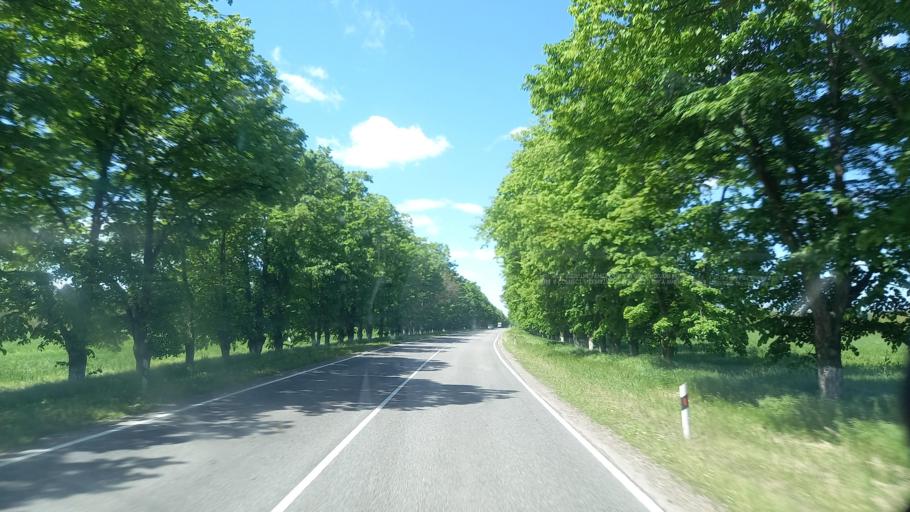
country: RU
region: Krasnodarskiy
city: Kazanskaya
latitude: 45.3712
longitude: 40.4443
